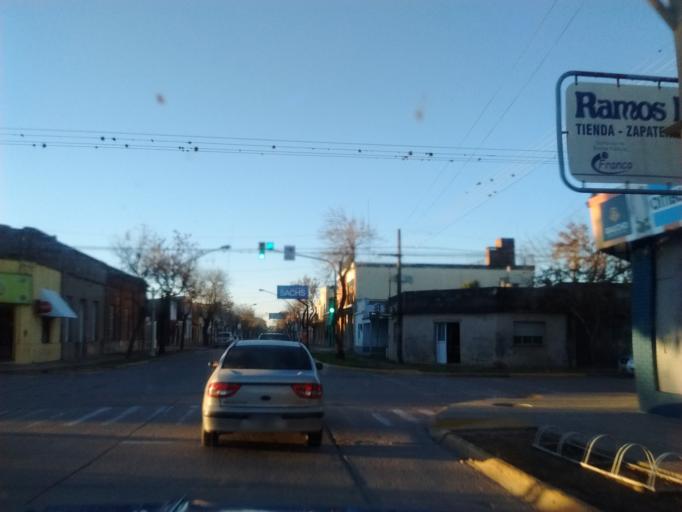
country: AR
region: Santa Fe
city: San Carlos Centro
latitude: -31.7327
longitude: -61.0943
